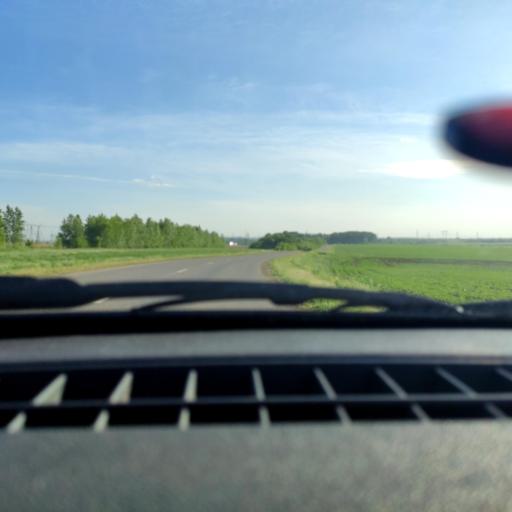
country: RU
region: Bashkortostan
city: Avdon
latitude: 54.4399
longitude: 55.8373
